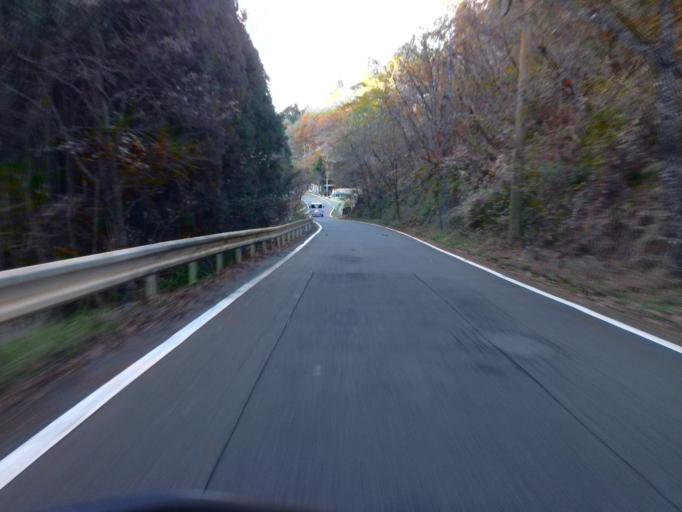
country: JP
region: Gifu
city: Mitake
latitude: 35.6044
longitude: 137.1973
